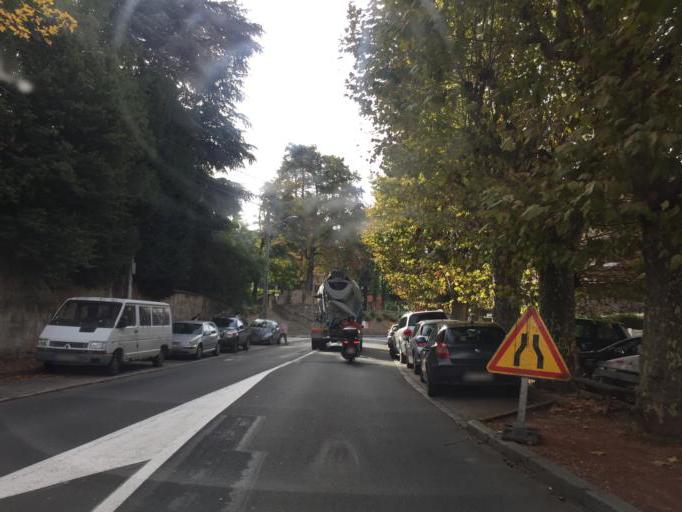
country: FR
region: Rhone-Alpes
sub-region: Departement du Rhone
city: Chasselay
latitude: 45.8736
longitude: 4.7721
